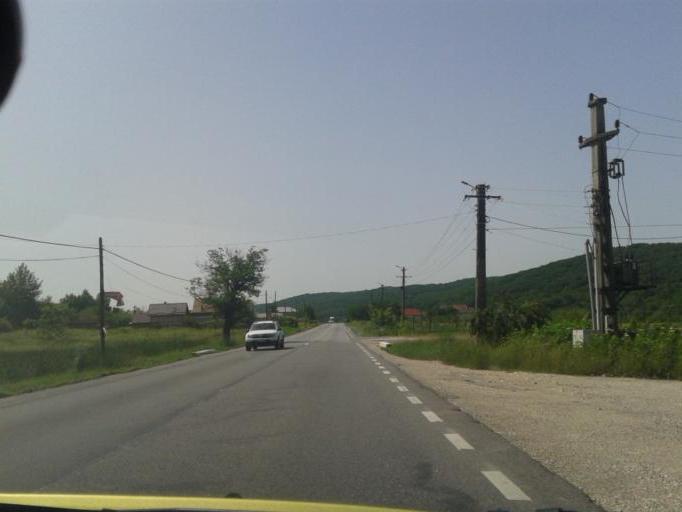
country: RO
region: Arges
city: Draganu-Olteni
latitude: 44.9193
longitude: 24.7211
